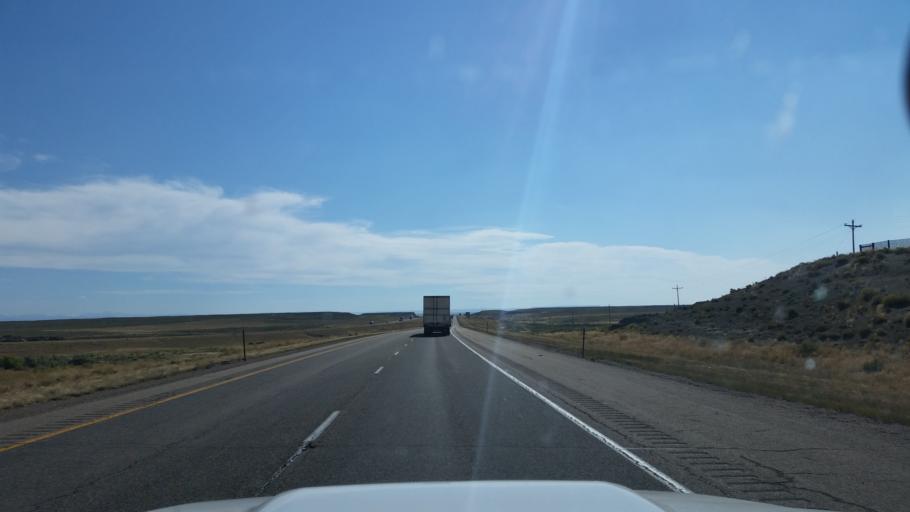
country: US
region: Wyoming
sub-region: Uinta County
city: Lyman
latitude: 41.4104
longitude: -110.1500
